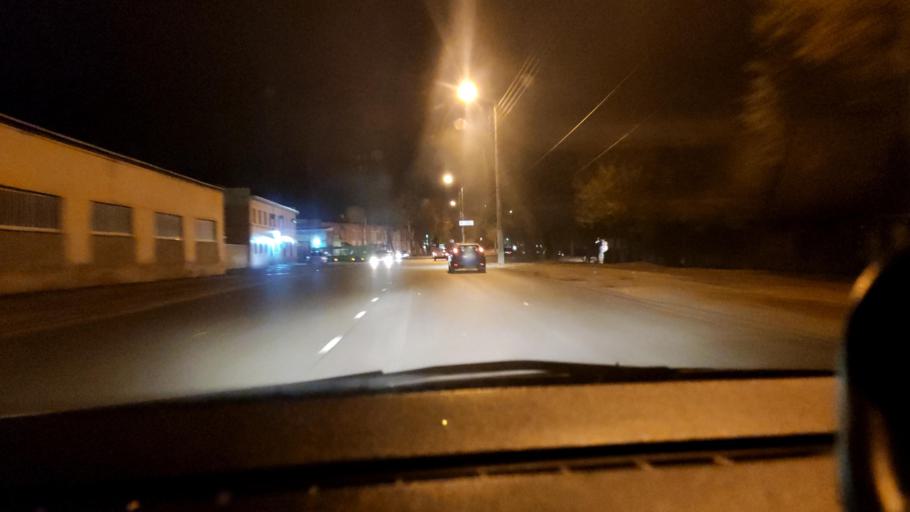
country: RU
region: Voronezj
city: Voronezh
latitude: 51.6269
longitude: 39.1762
